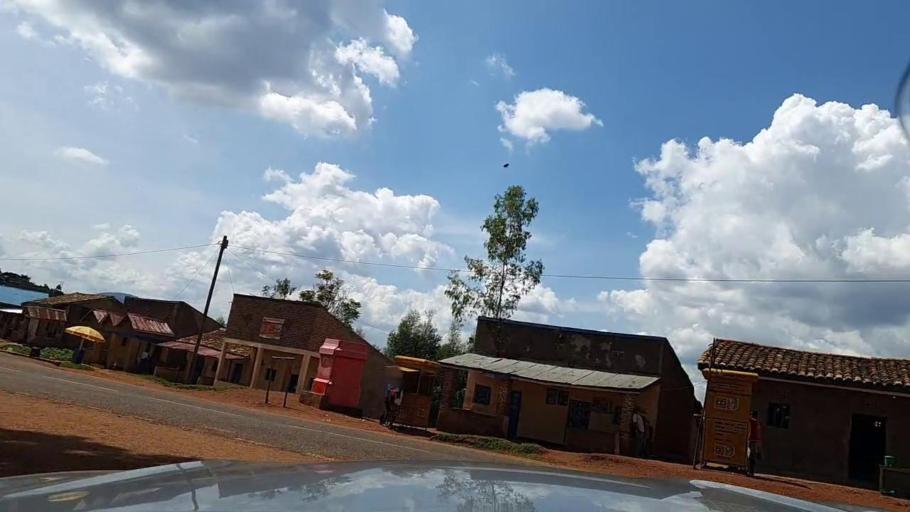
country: RW
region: Southern Province
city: Butare
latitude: -2.7442
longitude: 29.6961
